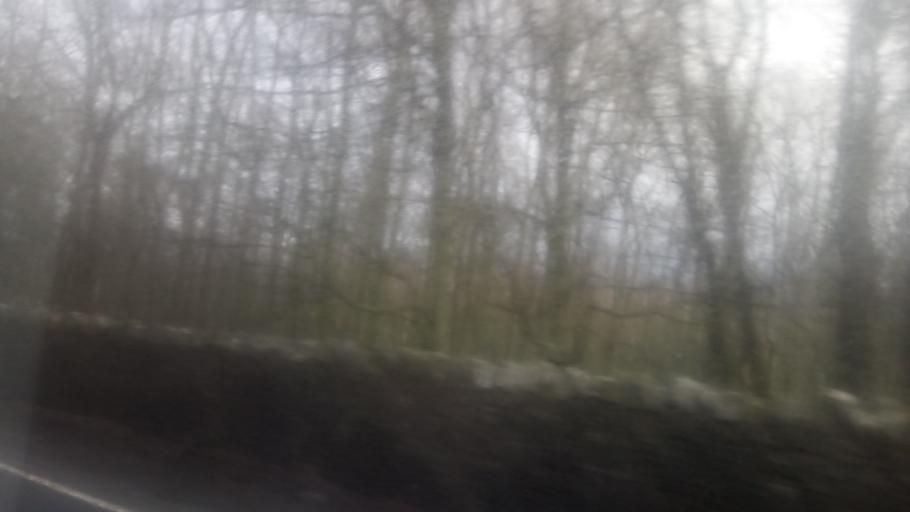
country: GB
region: Scotland
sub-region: The Scottish Borders
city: Lauder
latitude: 55.7307
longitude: -2.7638
